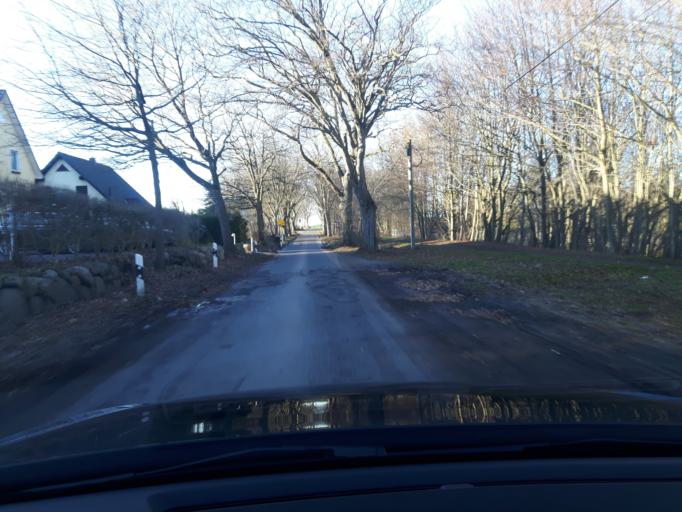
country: DE
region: Mecklenburg-Vorpommern
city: Putbus
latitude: 54.3575
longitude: 13.4450
